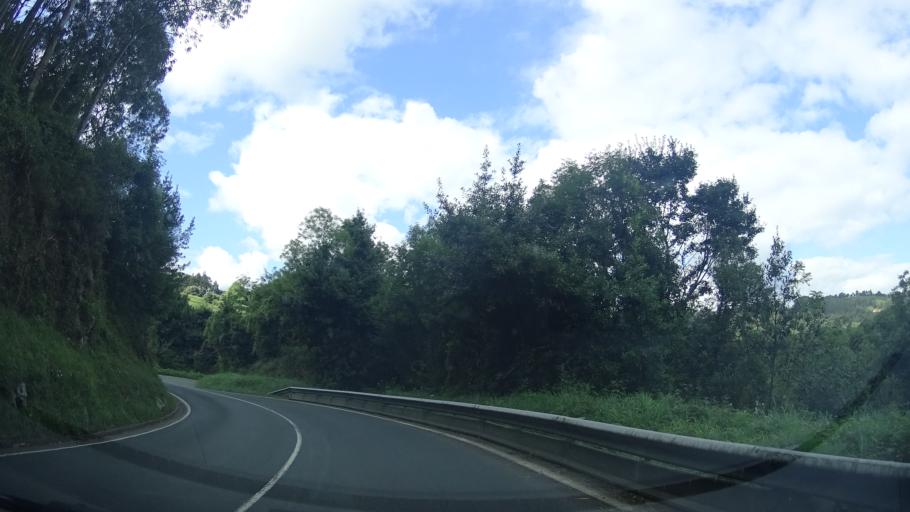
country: ES
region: Asturias
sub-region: Province of Asturias
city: Ribadesella
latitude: 43.4654
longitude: -5.1245
